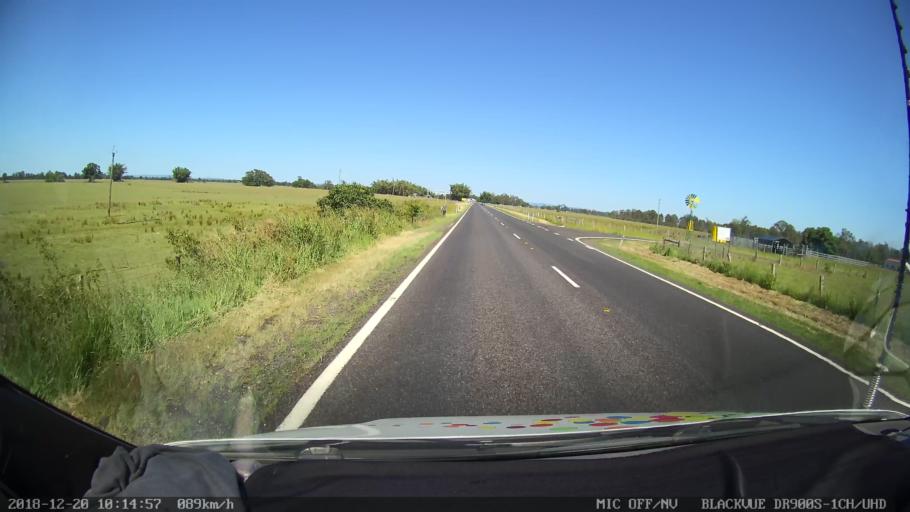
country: AU
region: New South Wales
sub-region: Richmond Valley
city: Casino
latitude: -28.8688
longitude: 153.1071
